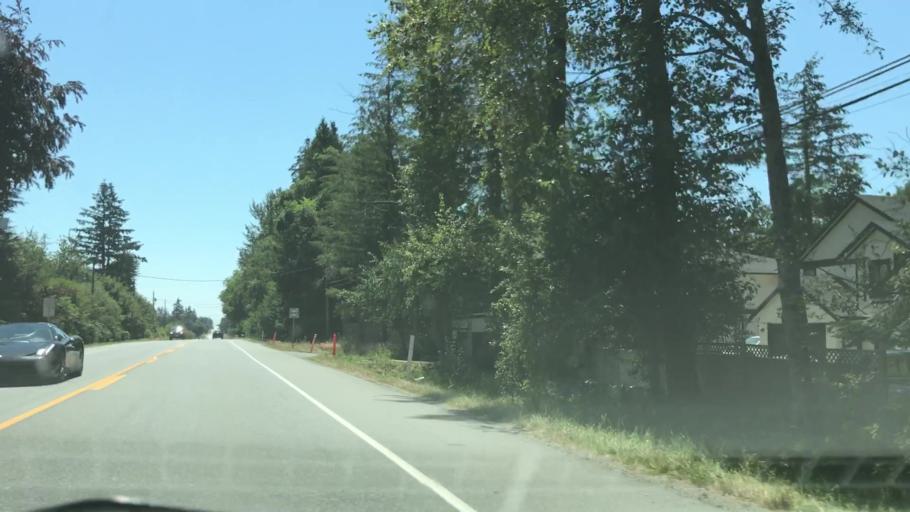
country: CA
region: British Columbia
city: Aldergrove
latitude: 49.0454
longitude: -122.4926
